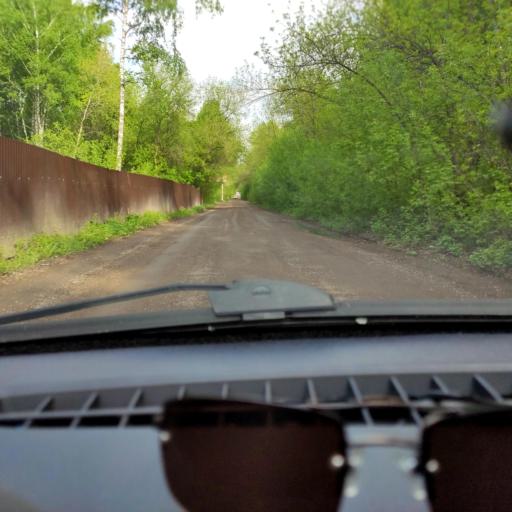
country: RU
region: Bashkortostan
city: Ufa
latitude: 54.6982
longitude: 55.9350
